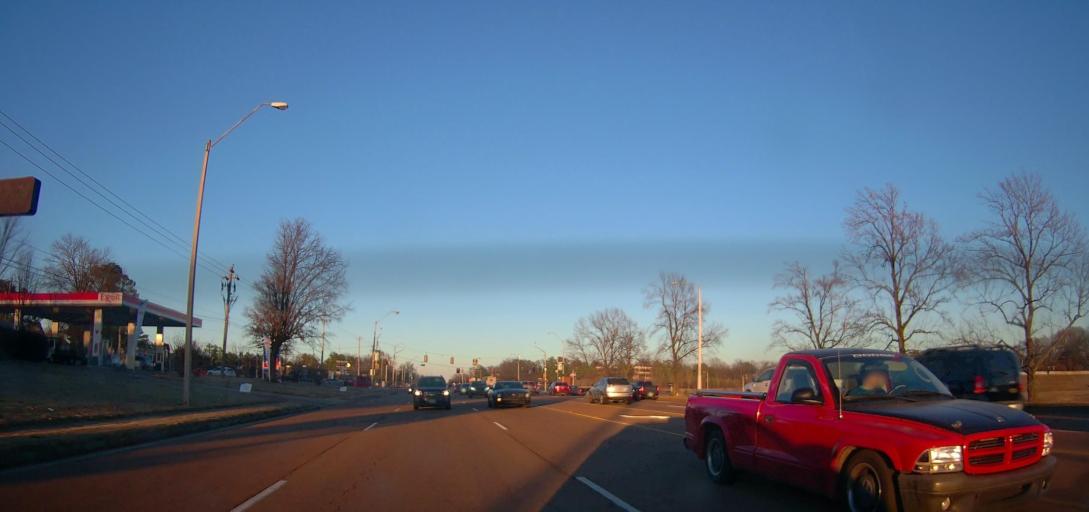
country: US
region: Tennessee
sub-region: Shelby County
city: Bartlett
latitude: 35.2206
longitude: -89.9099
